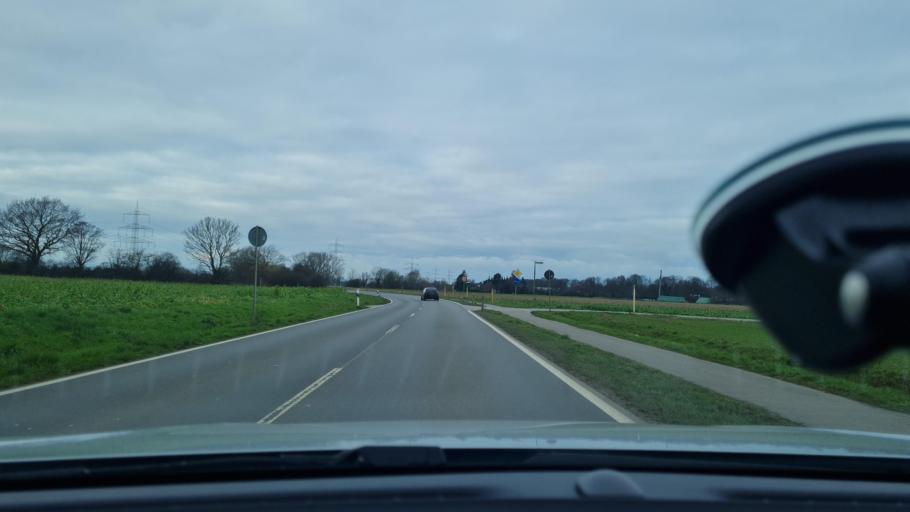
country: DE
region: North Rhine-Westphalia
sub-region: Regierungsbezirk Dusseldorf
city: Voerde
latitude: 51.5851
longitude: 6.6771
